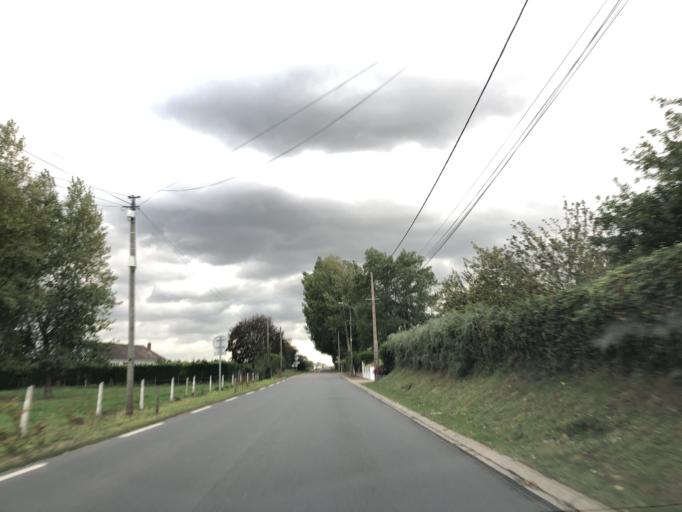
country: FR
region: Haute-Normandie
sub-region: Departement de la Seine-Maritime
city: Eu
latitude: 50.0751
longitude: 1.4349
